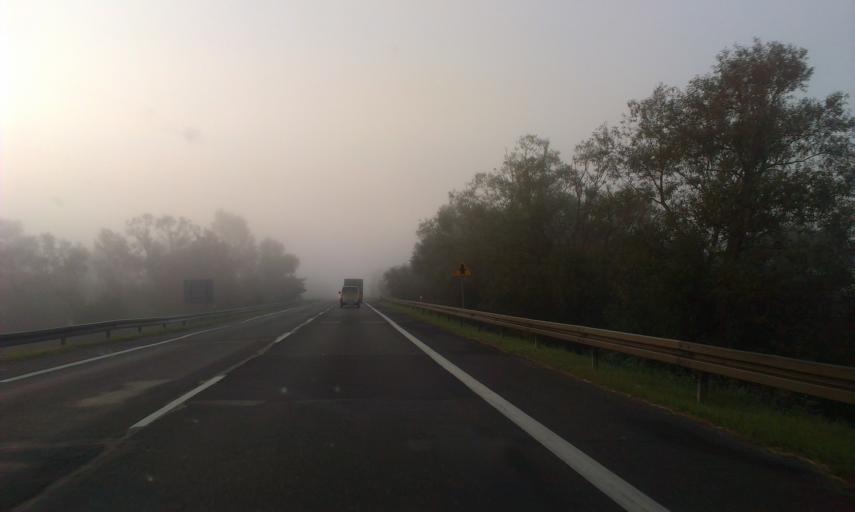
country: PL
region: Kujawsko-Pomorskie
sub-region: Powiat chelminski
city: Chelmno
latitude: 53.3884
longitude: 18.4085
